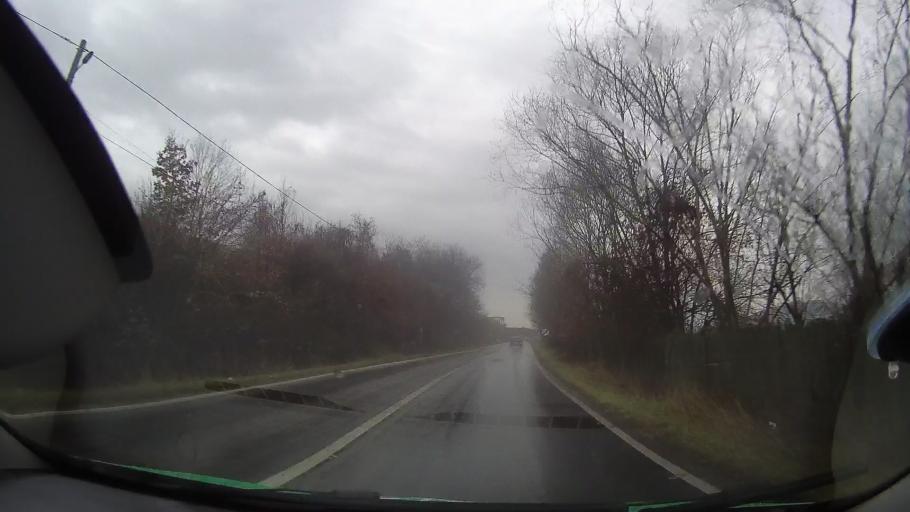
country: RO
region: Bihor
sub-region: Comuna Rabagani
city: Rabagani
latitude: 46.7523
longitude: 22.2101
